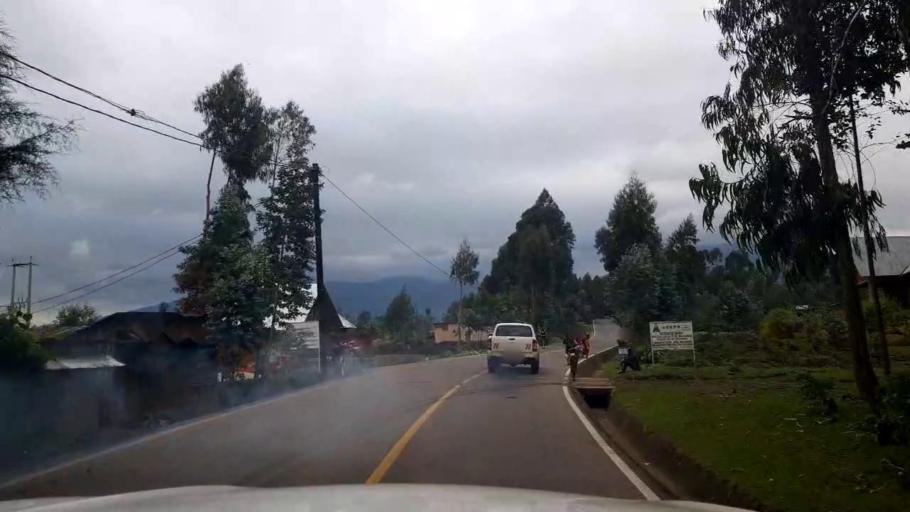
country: RW
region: Northern Province
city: Musanze
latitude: -1.4361
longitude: 29.5543
